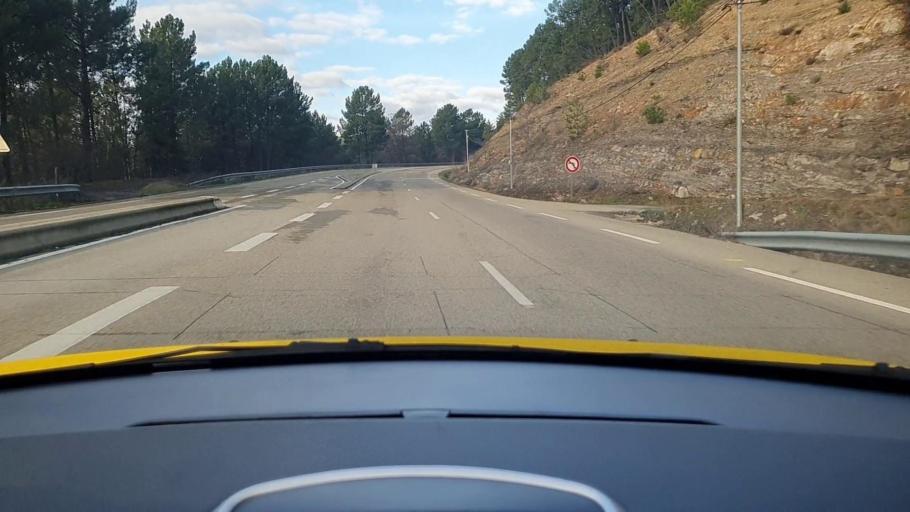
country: FR
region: Languedoc-Roussillon
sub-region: Departement du Gard
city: Les Salles-du-Gardon
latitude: 44.2591
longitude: 4.0398
